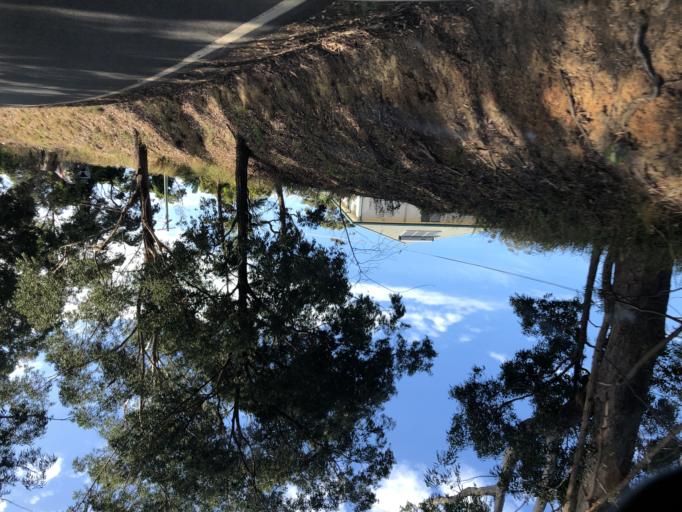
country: AU
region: New South Wales
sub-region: Coffs Harbour
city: Coffs Harbour
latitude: -30.2609
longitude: 153.1325
